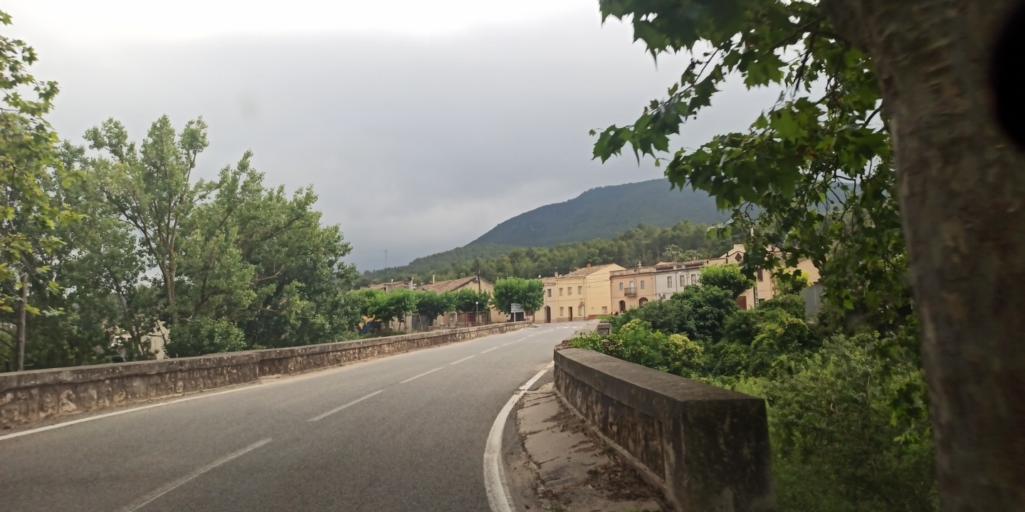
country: ES
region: Catalonia
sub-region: Provincia de Tarragona
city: la Bisbal del Penedes
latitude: 41.3687
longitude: 1.5019
